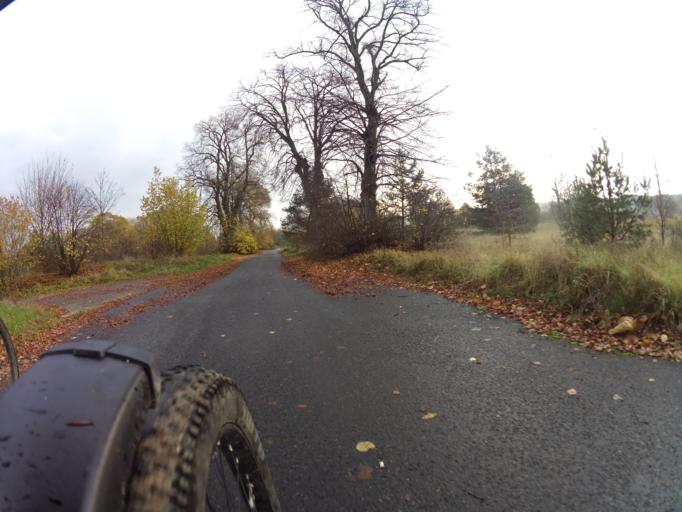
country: PL
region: Pomeranian Voivodeship
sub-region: Powiat wejherowski
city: Gniewino
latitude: 54.7120
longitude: 18.0967
